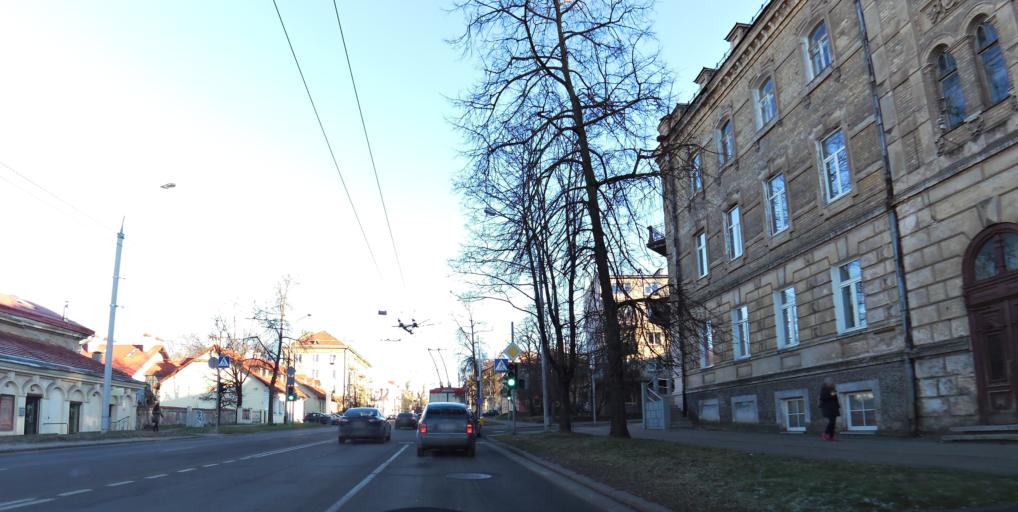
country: LT
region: Vilnius County
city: Naujamiestis
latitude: 54.6807
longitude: 25.2622
